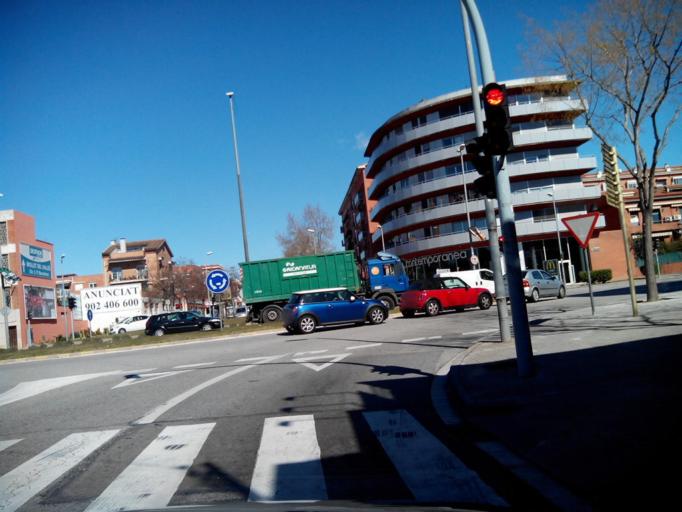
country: ES
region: Catalonia
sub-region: Provincia de Barcelona
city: Granollers
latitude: 41.5957
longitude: 2.2880
